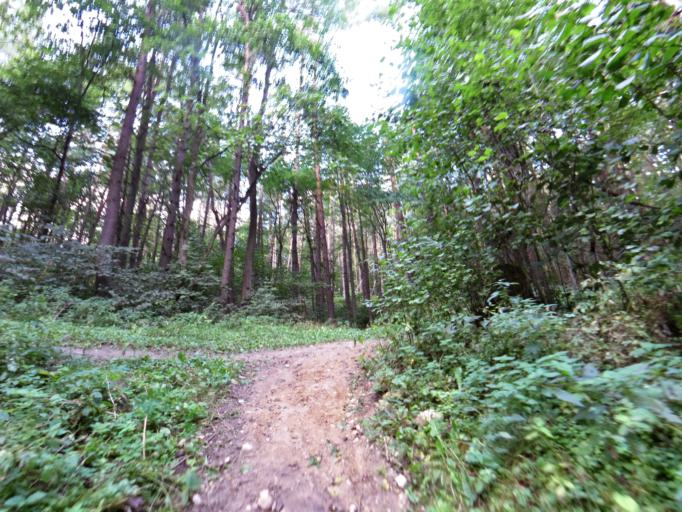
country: LT
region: Vilnius County
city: Justiniskes
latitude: 54.6919
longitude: 25.2294
